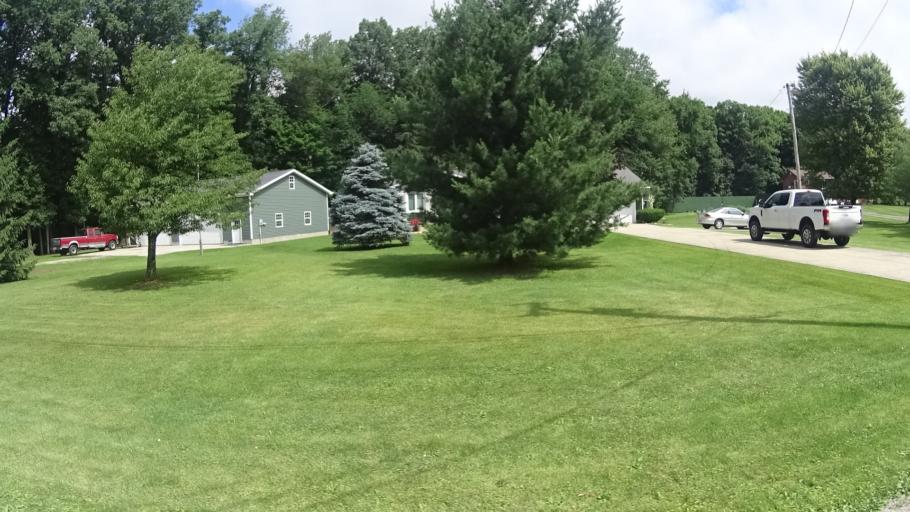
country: US
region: Ohio
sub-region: Huron County
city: Wakeman
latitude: 41.3201
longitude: -82.3693
